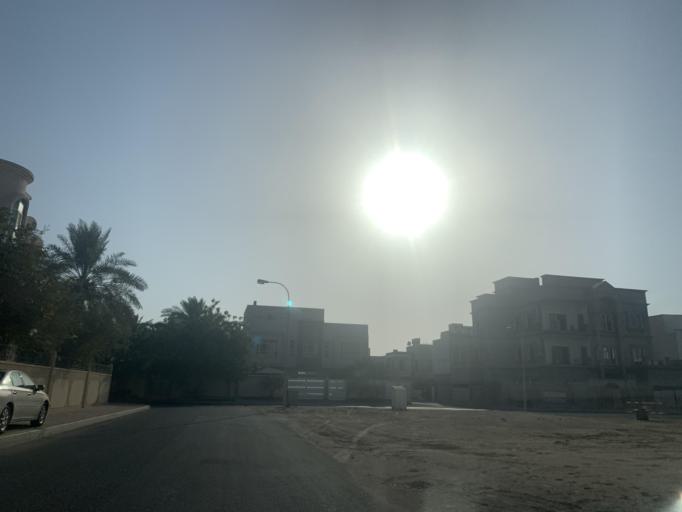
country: BH
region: Manama
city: Jidd Hafs
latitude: 26.2111
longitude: 50.5306
